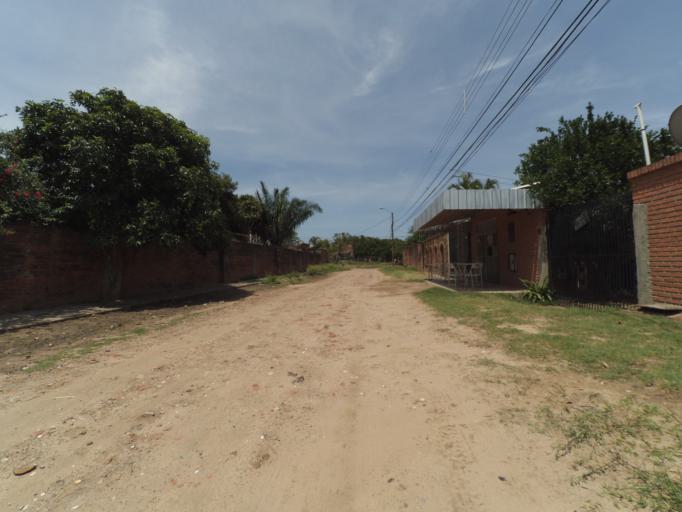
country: BO
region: Santa Cruz
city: Santa Cruz de la Sierra
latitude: -17.8235
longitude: -63.2242
